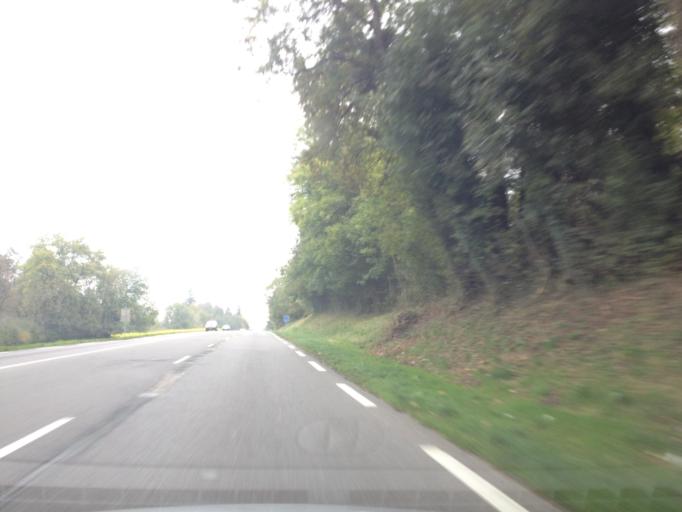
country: FR
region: Rhone-Alpes
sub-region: Departement de la Haute-Savoie
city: Viuz-la-Chiesaz
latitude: 45.8477
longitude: 6.0595
